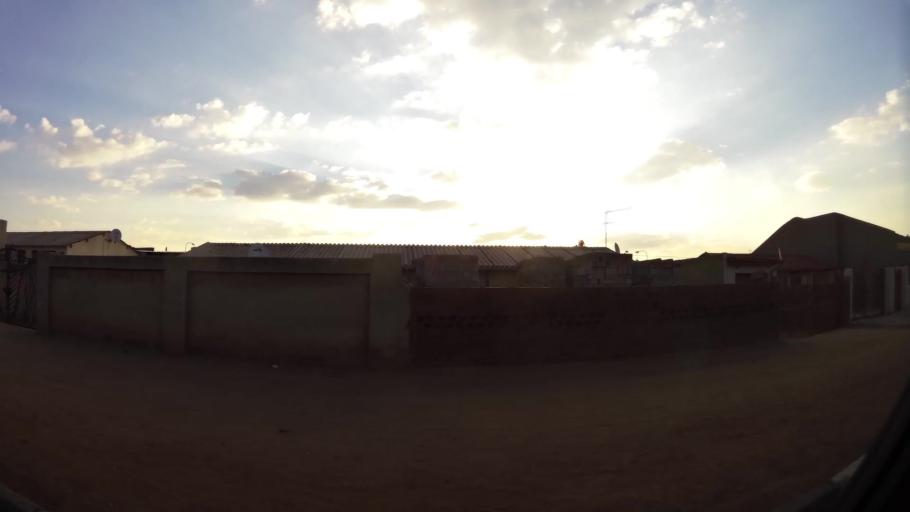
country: ZA
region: Gauteng
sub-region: City of Johannesburg Metropolitan Municipality
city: Roodepoort
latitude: -26.2109
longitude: 27.8951
